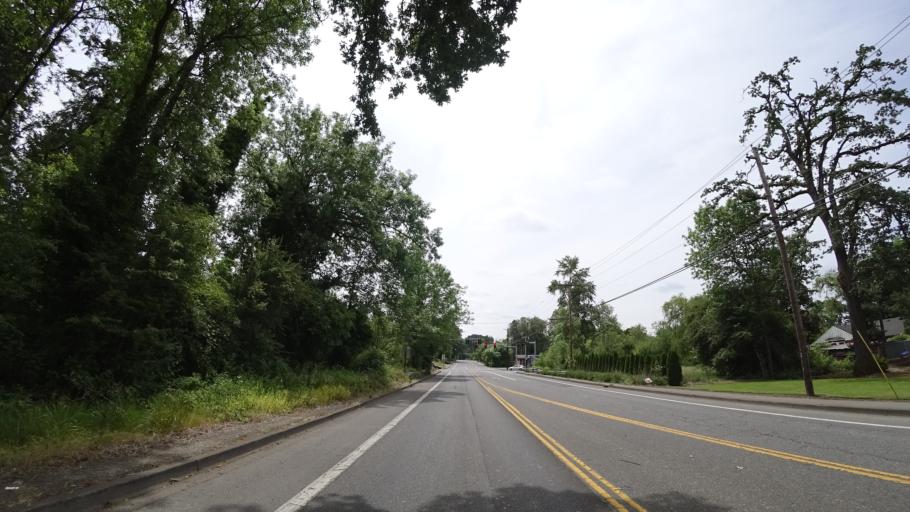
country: US
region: Oregon
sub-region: Washington County
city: Metzger
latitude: 45.4451
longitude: -122.7656
